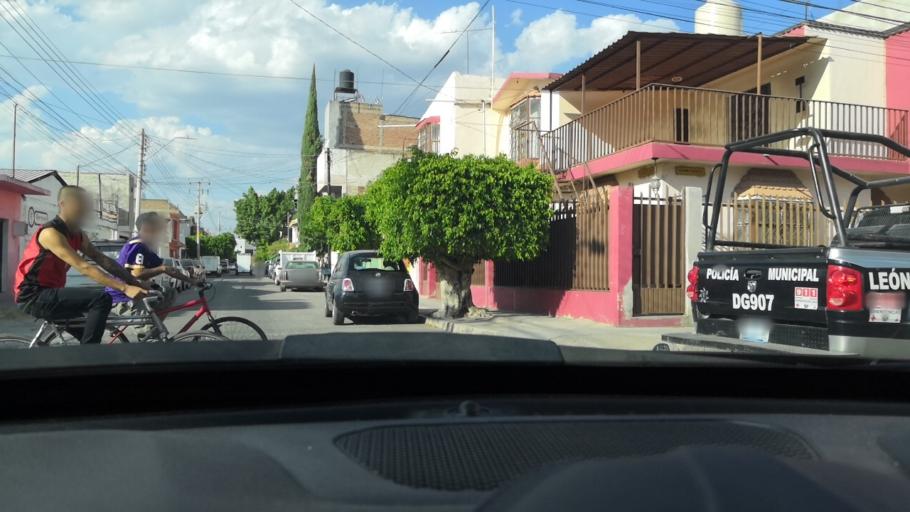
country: MX
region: Guanajuato
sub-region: Leon
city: San Jose de Duran (Los Troncoso)
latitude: 21.0944
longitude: -101.6519
